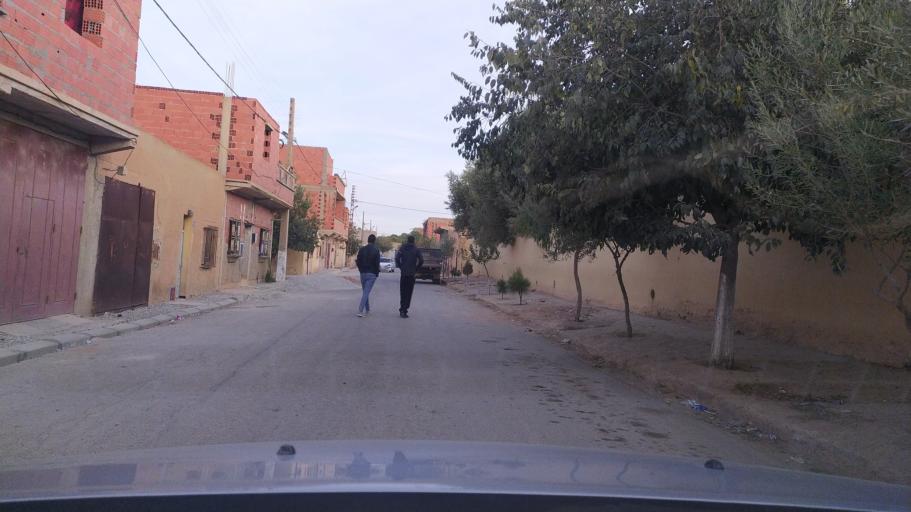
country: DZ
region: Tiaret
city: Frenda
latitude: 34.9000
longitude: 1.2353
